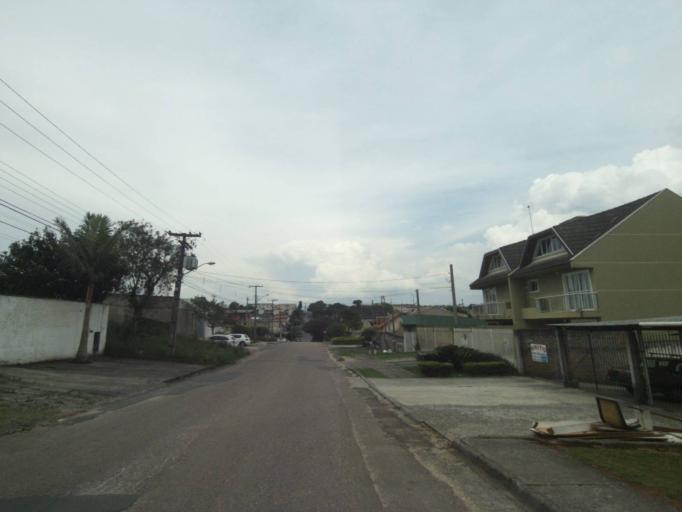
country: BR
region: Parana
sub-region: Pinhais
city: Pinhais
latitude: -25.4006
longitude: -49.2117
